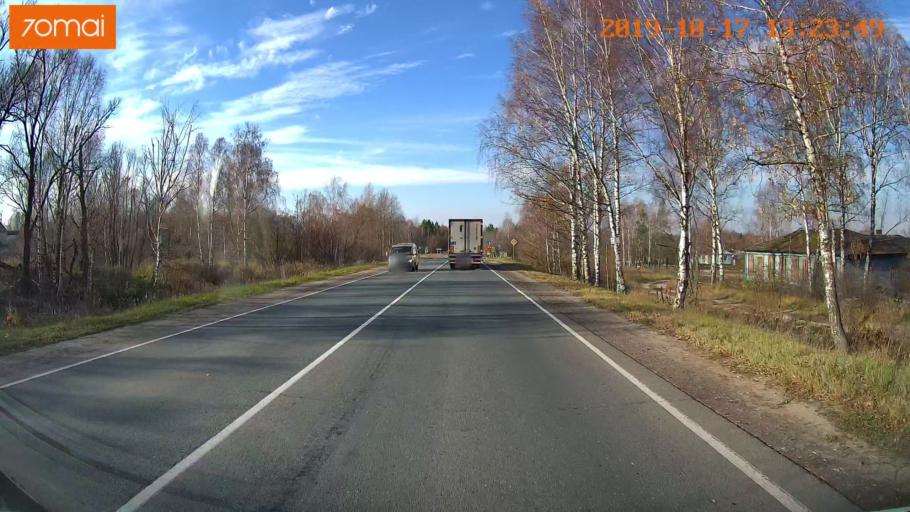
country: RU
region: Rjazan
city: Gus'-Zheleznyy
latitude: 55.0916
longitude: 40.9737
